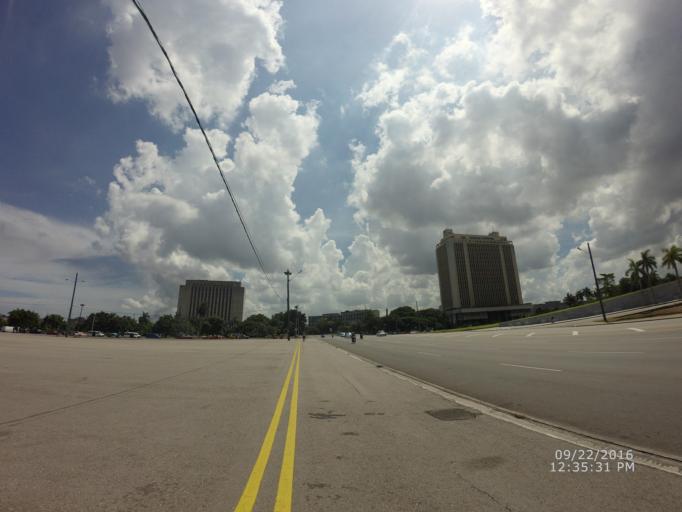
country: CU
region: La Habana
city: Havana
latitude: 23.1241
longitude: -82.3857
